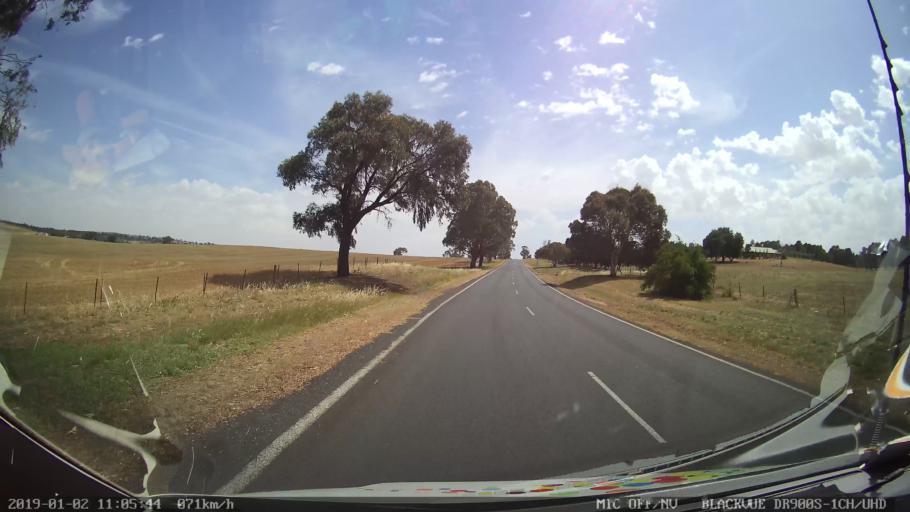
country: AU
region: New South Wales
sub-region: Young
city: Young
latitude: -34.5614
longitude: 148.3538
